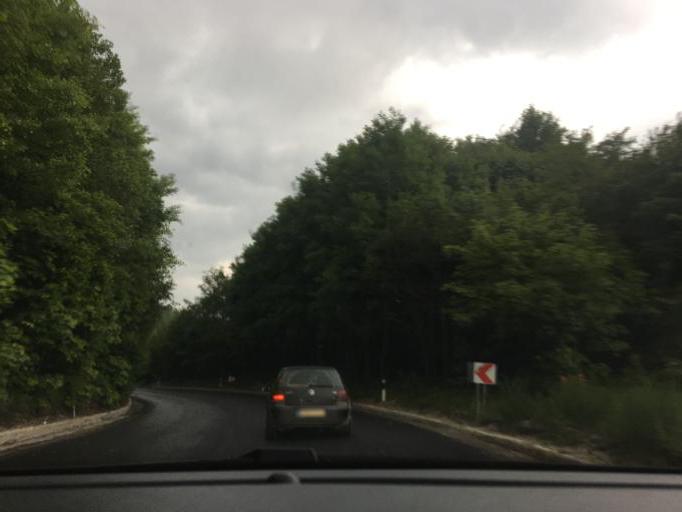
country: MK
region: Gostivar
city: Vrutok
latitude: 41.6782
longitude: 20.8495
